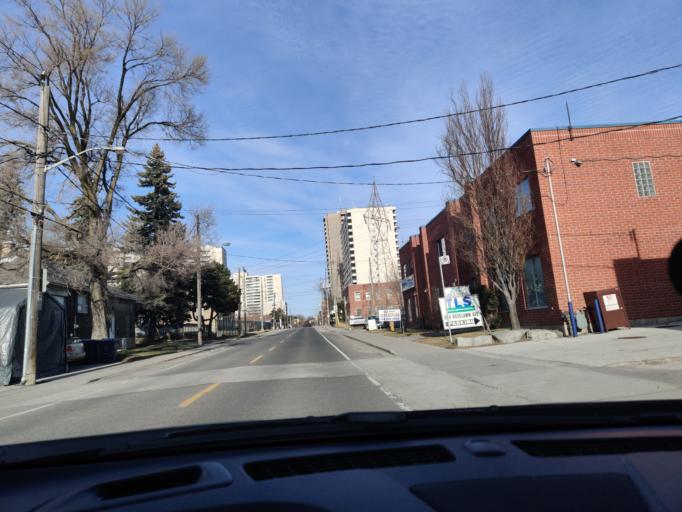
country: CA
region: Ontario
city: Toronto
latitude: 43.7015
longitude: -79.4444
